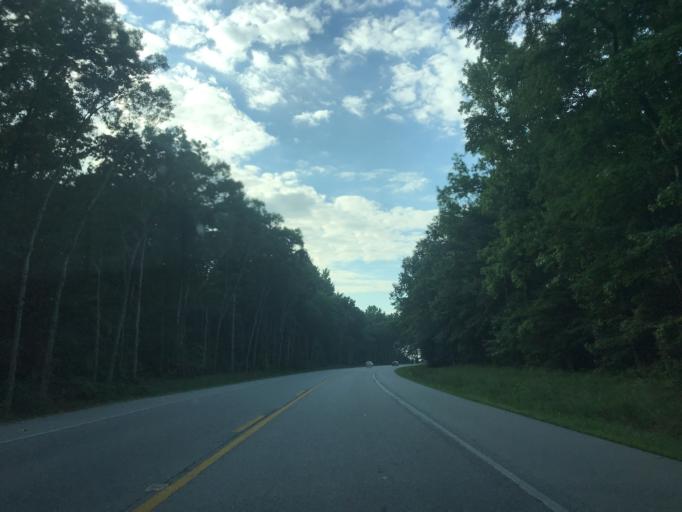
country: US
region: Maryland
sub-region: Caroline County
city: Federalsburg
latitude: 38.7363
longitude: -75.7913
